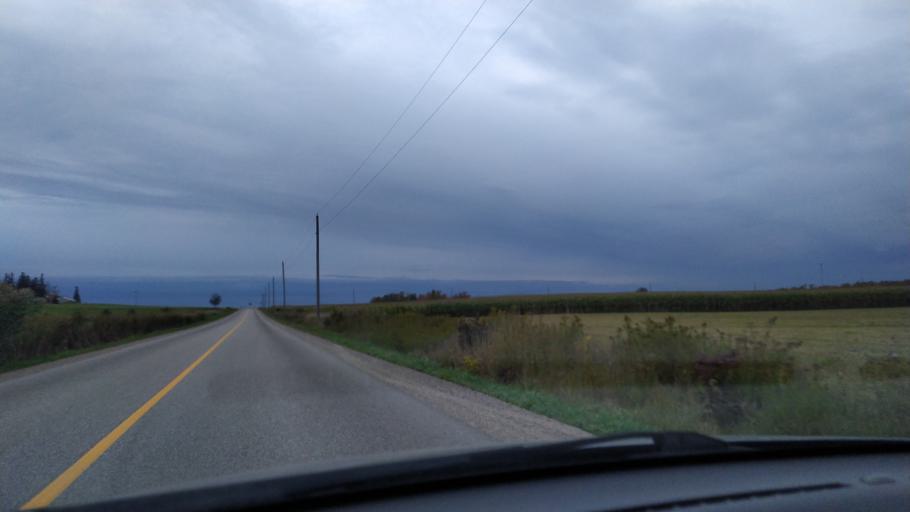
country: CA
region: Ontario
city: Waterloo
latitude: 43.5133
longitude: -80.7496
